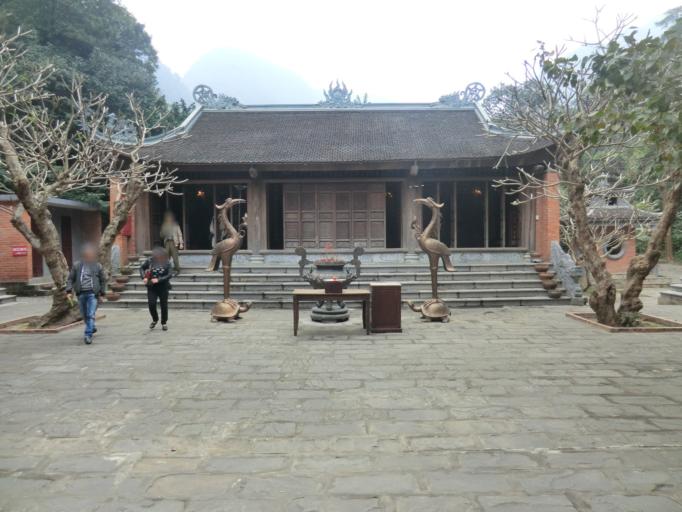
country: VN
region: Ninh Binh
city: Thi Tran Thien Ton
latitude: 20.2684
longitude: 105.9051
